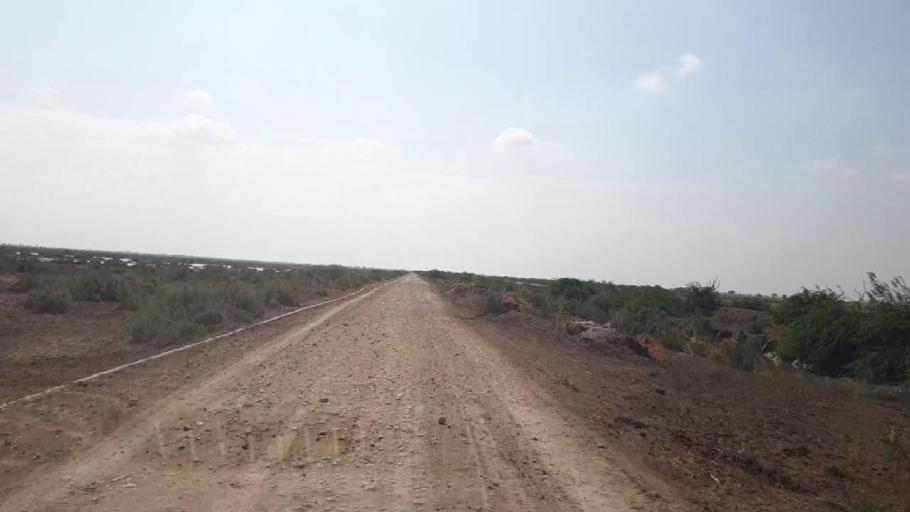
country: PK
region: Sindh
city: Badin
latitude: 24.5096
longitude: 68.6081
